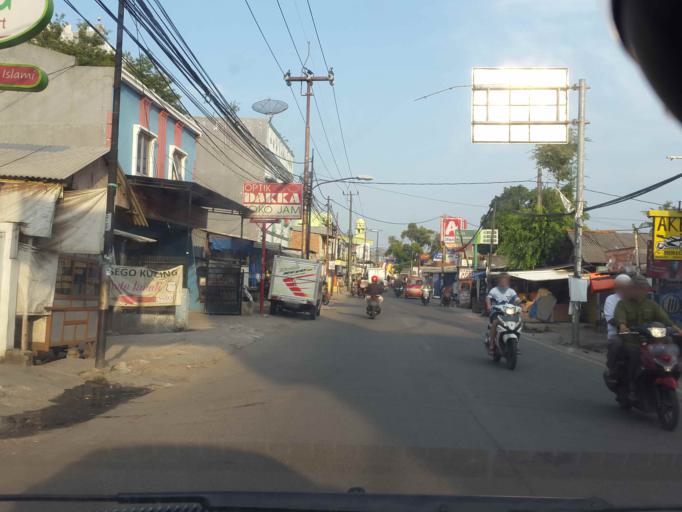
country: ID
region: Banten
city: South Tangerang
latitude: -6.2626
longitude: 106.7308
